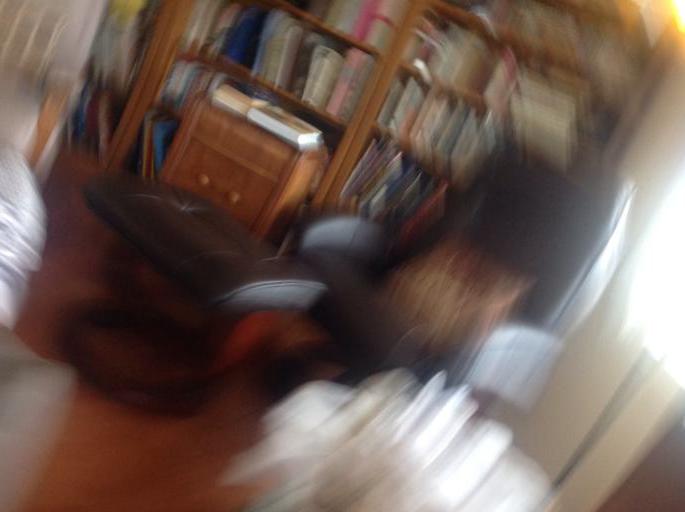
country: US
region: New York
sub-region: Monroe County
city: Hilton
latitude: 43.2907
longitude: -77.7621
